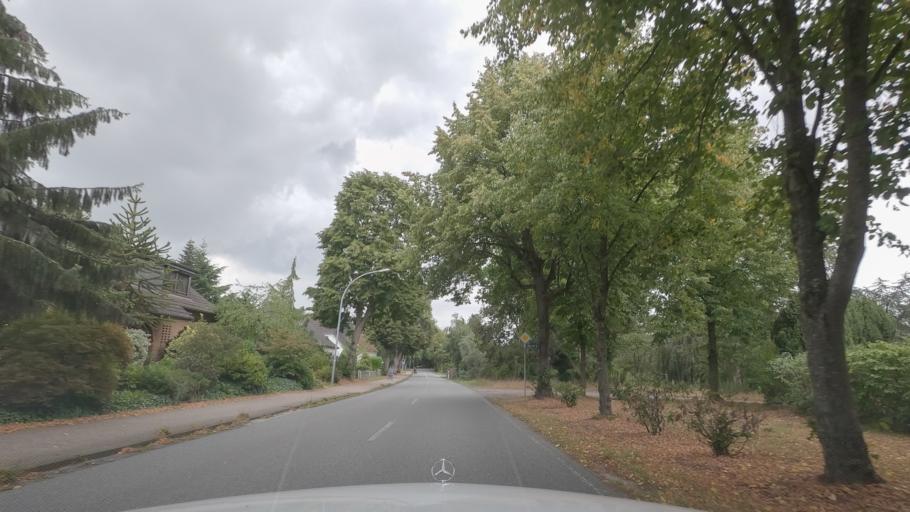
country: DE
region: Lower Saxony
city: Neuenkirchen
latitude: 53.2306
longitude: 8.5289
